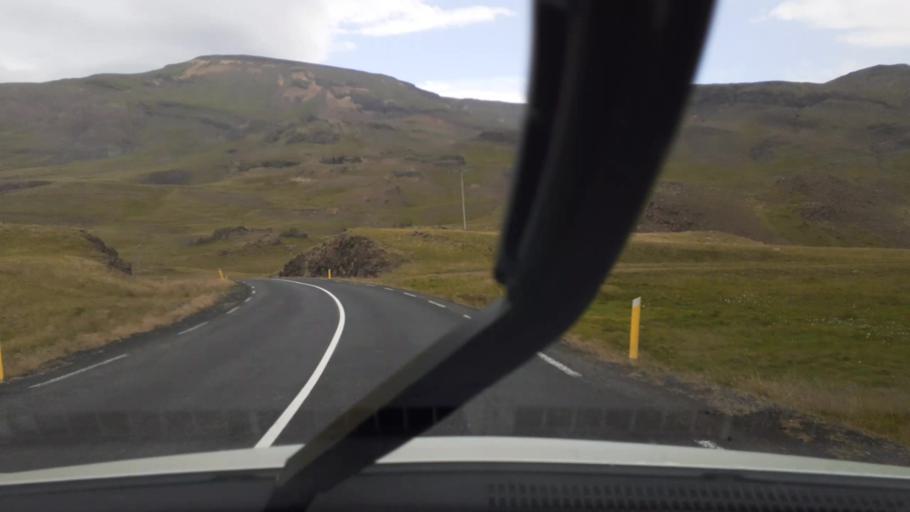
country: IS
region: Capital Region
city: Mosfellsbaer
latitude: 64.3951
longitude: -21.4351
